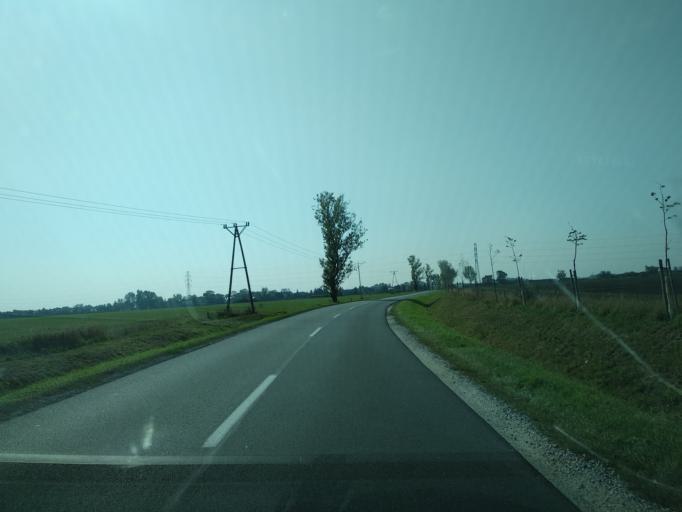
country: PL
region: Lower Silesian Voivodeship
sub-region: Powiat wroclawski
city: Zerniki Wroclawskie
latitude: 51.0417
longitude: 17.0297
